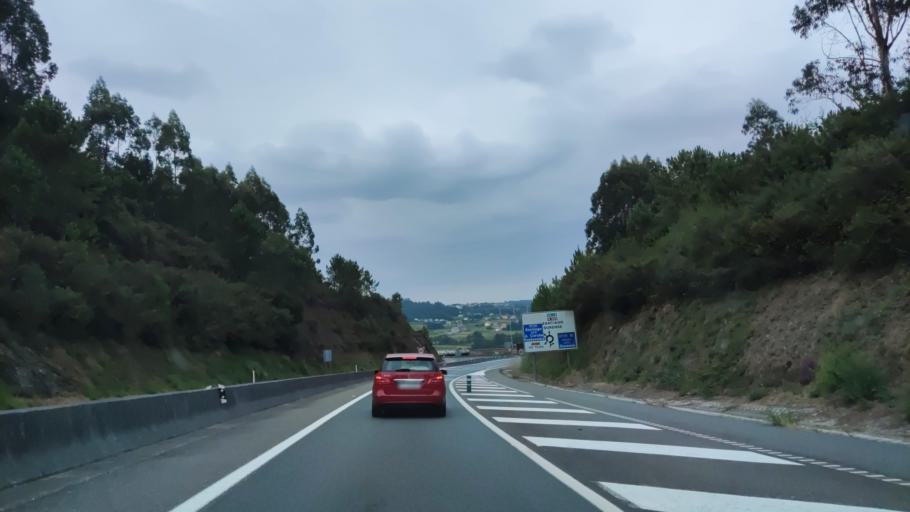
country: ES
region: Galicia
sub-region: Provincia da Coruna
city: Santiago de Compostela
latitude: 42.8355
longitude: -8.5295
